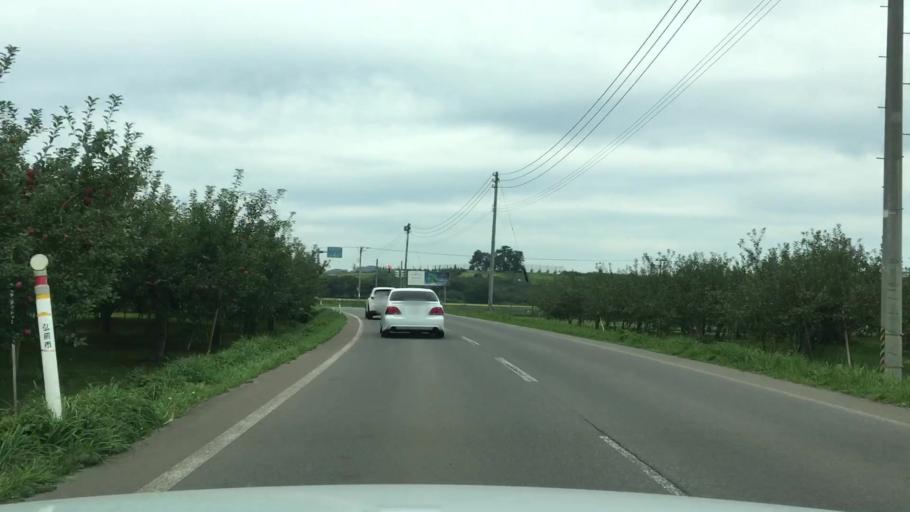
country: JP
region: Aomori
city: Hirosaki
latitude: 40.6583
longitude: 140.4191
